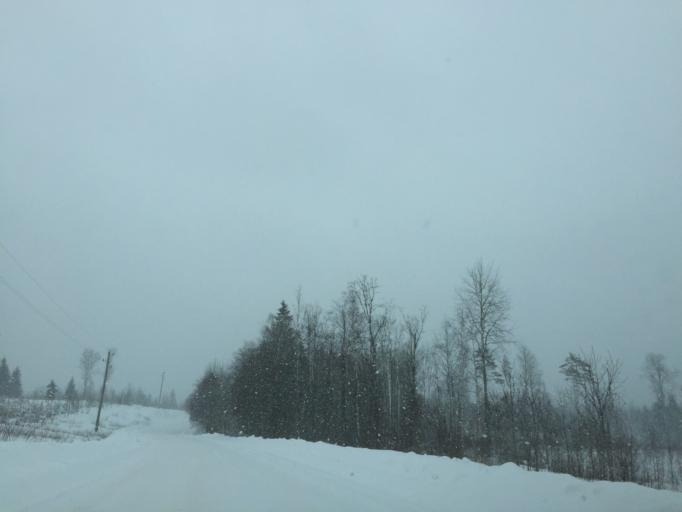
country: LV
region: Amatas Novads
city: Drabesi
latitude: 57.0795
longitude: 25.3424
